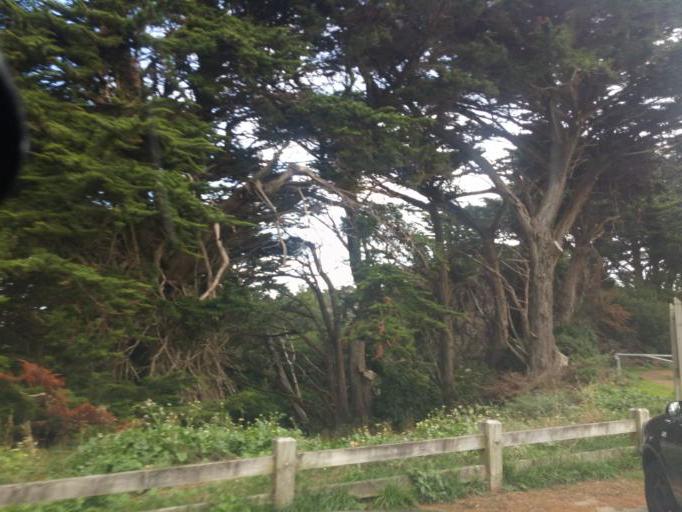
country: NZ
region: Wellington
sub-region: Wellington City
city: Kelburn
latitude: -41.2664
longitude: 174.7720
